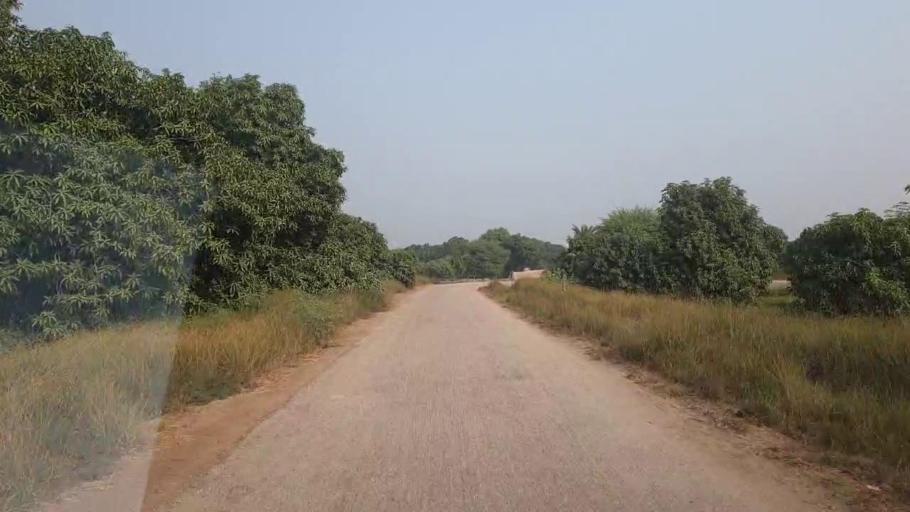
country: PK
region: Sindh
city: Tando Jam
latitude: 25.3377
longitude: 68.5180
